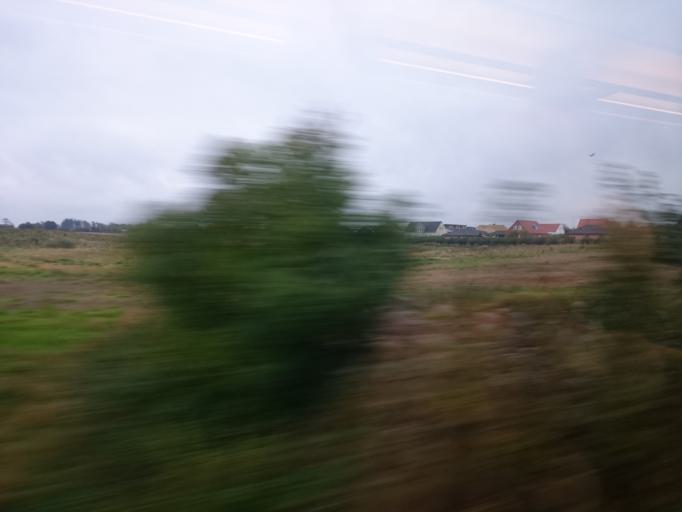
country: DK
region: Central Jutland
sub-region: Arhus Kommune
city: Marslet
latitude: 56.0756
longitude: 10.1534
